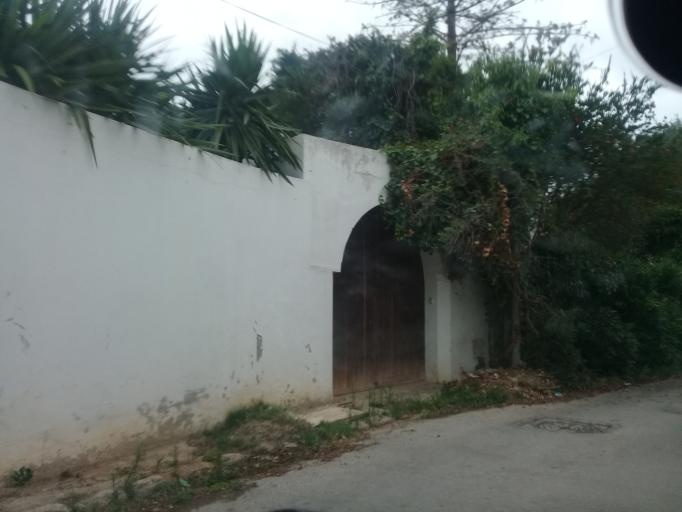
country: TN
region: Tunis
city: Sidi Bou Said
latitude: 36.8702
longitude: 10.3395
